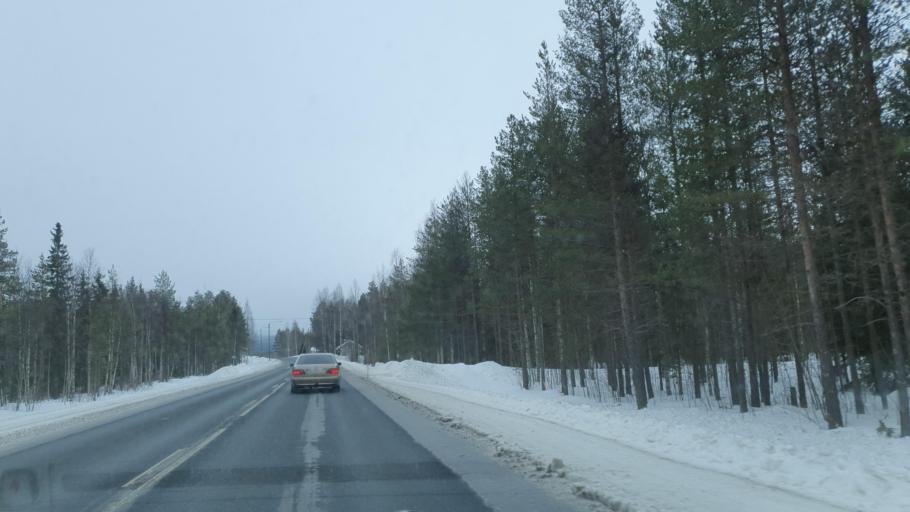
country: FI
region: Lapland
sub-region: Torniolaakso
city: Pello
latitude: 66.7285
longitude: 23.9132
